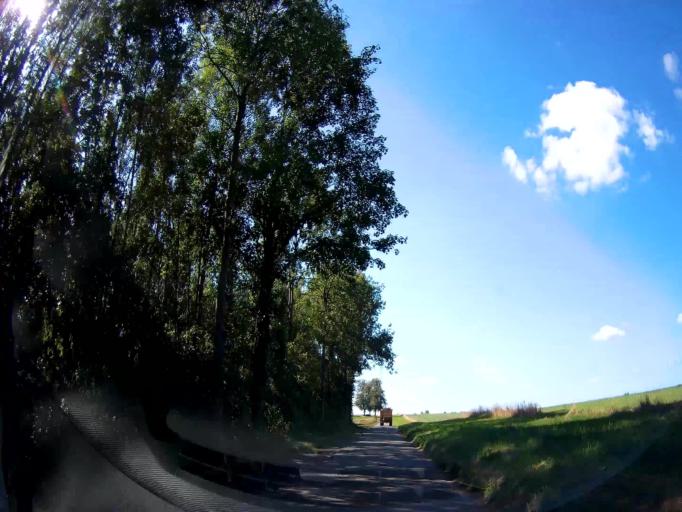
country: BE
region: Wallonia
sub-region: Province de Namur
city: Houyet
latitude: 50.2347
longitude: 4.9719
